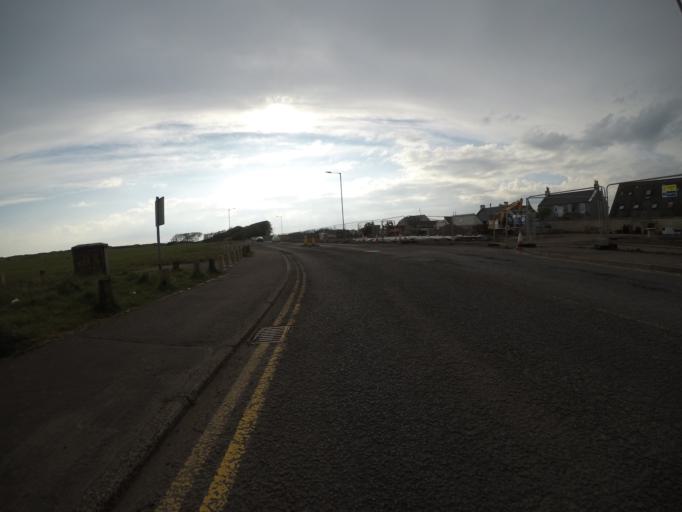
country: GB
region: Scotland
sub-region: North Ayrshire
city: Irvine
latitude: 55.6072
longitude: -4.6839
